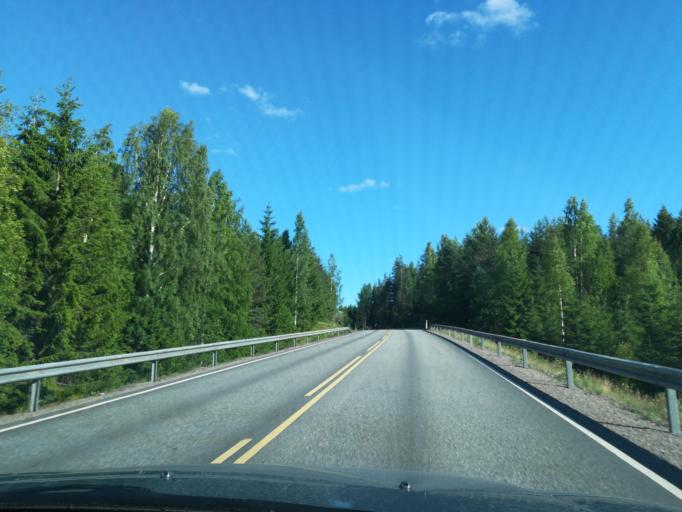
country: FI
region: South Karelia
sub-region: Imatra
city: Ruokolahti
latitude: 61.3609
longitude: 28.7020
